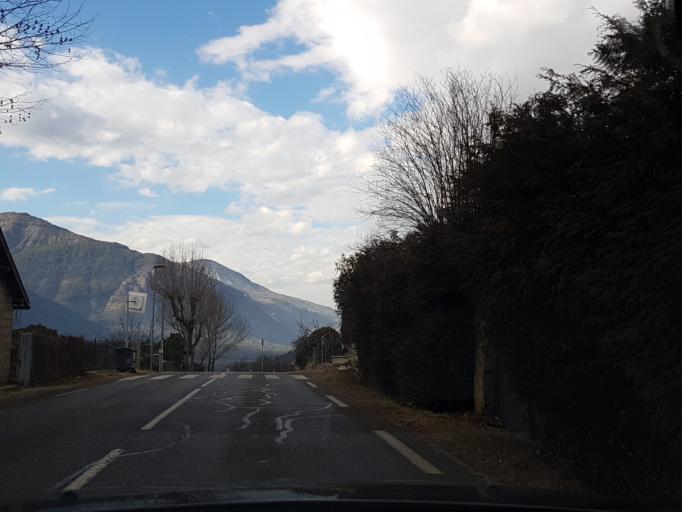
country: FR
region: Provence-Alpes-Cote d'Azur
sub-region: Departement des Hautes-Alpes
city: Tallard
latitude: 44.4676
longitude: 6.1611
